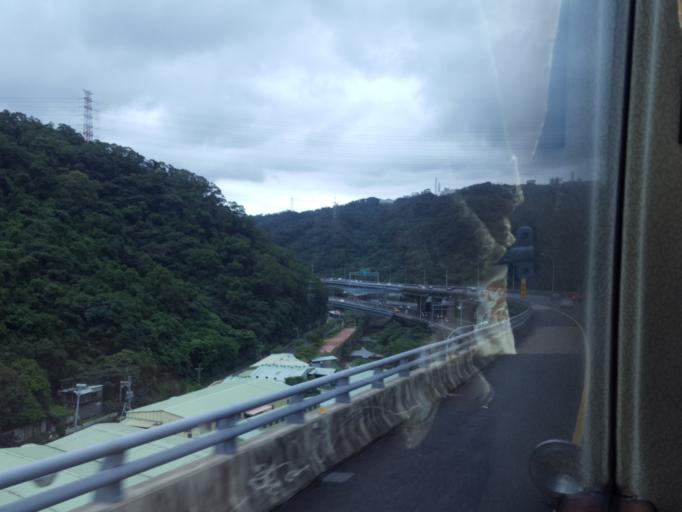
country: TW
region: Taipei
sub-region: Taipei
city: Banqiao
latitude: 25.0569
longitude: 121.4000
